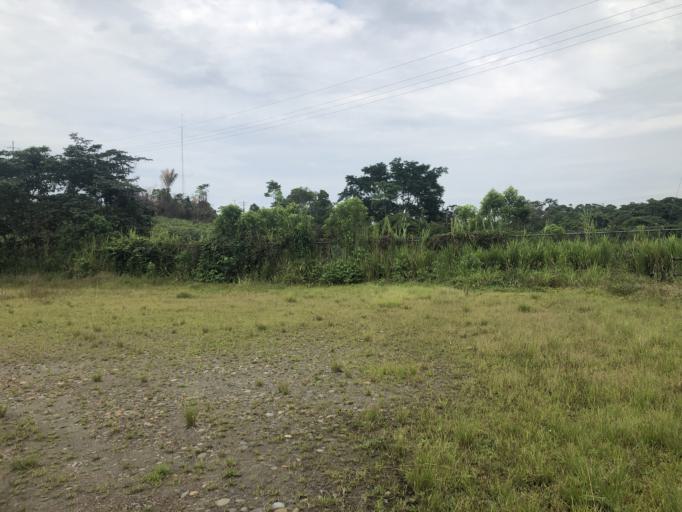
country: EC
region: Orellana
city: Boca Suno
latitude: -0.9871
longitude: -76.9308
